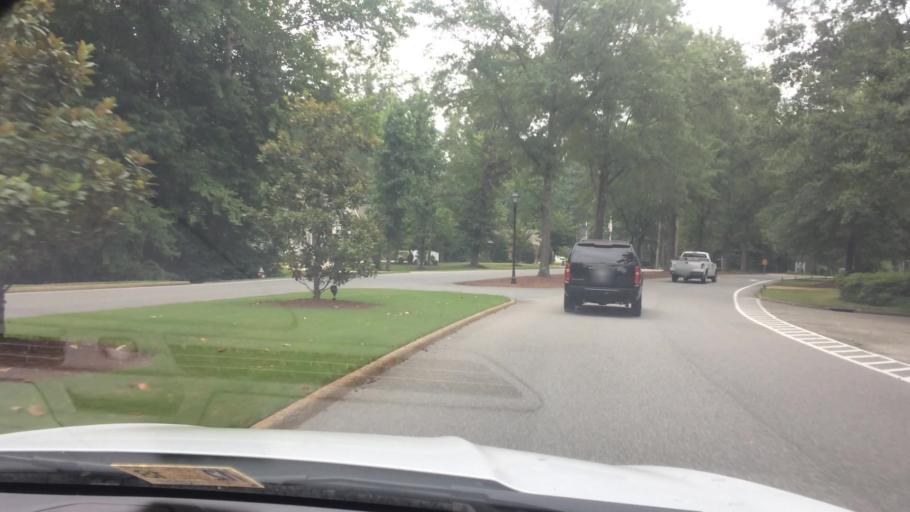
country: US
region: Virginia
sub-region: James City County
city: Williamsburg
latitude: 37.3123
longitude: -76.7752
